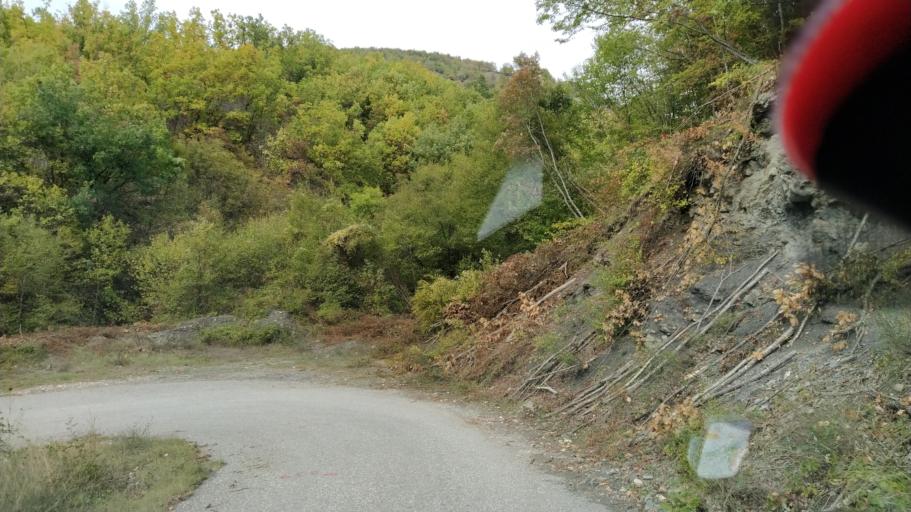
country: MK
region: Strumica
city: Veljusa
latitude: 41.5120
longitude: 22.4857
